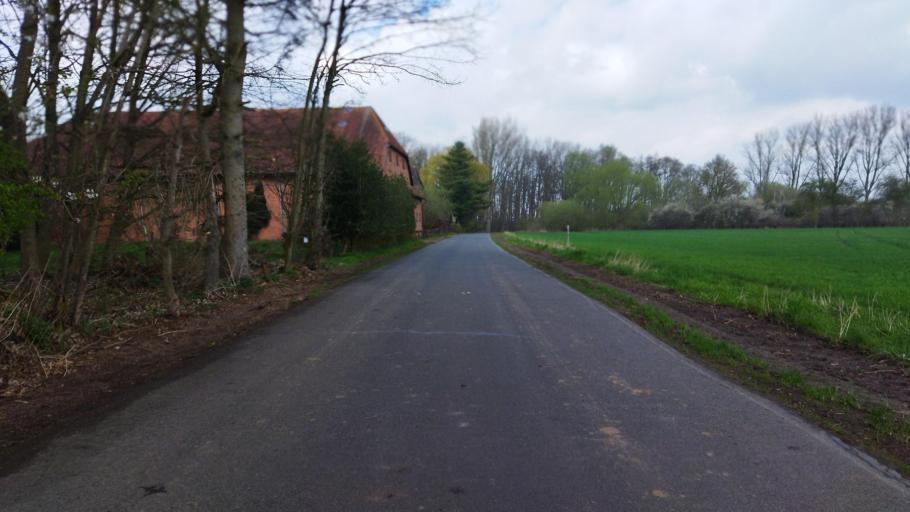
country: DE
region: Lower Saxony
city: Hilgermissen
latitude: 52.8312
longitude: 9.1901
